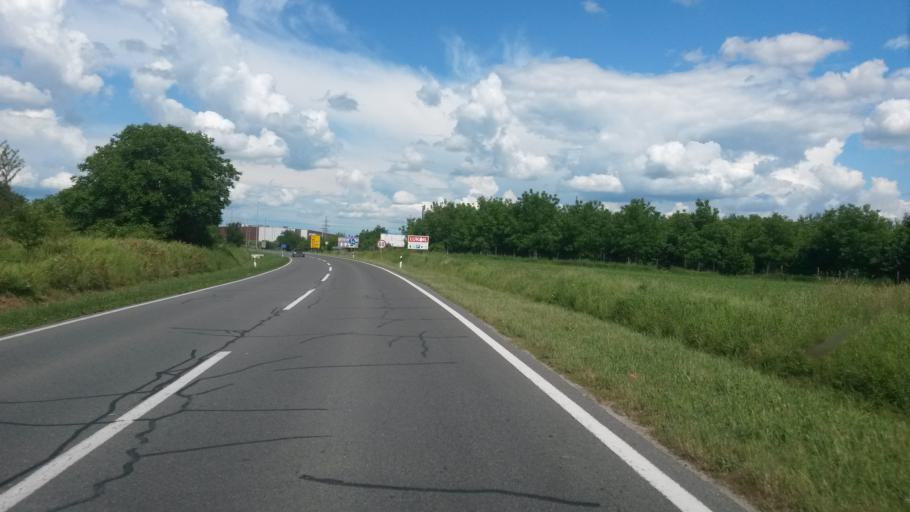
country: HR
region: Osjecko-Baranjska
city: Visnjevac
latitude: 45.5499
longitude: 18.6273
